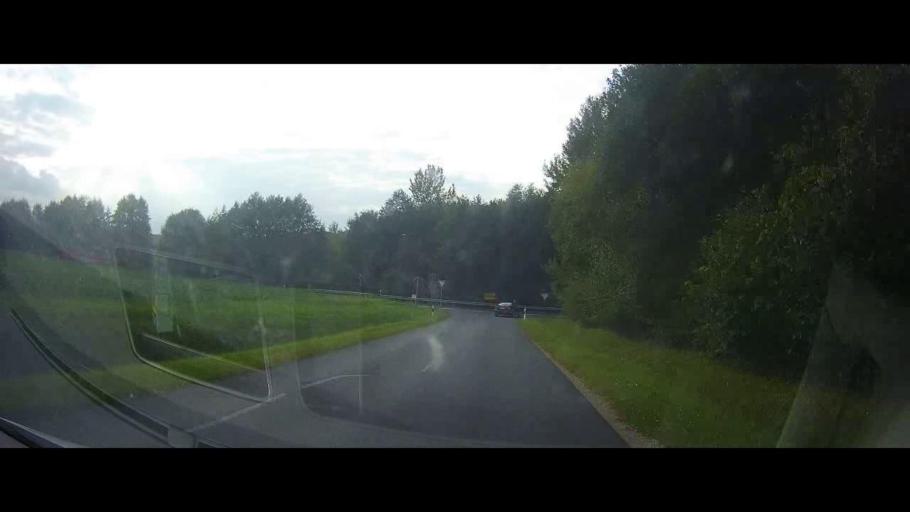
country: DE
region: Lower Saxony
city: Adelebsen
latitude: 51.5555
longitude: 9.7890
